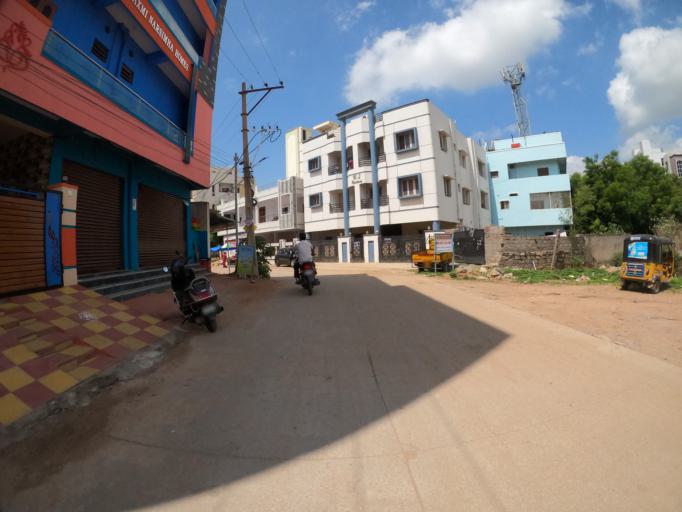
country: IN
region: Telangana
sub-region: Hyderabad
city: Hyderabad
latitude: 17.3619
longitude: 78.3862
